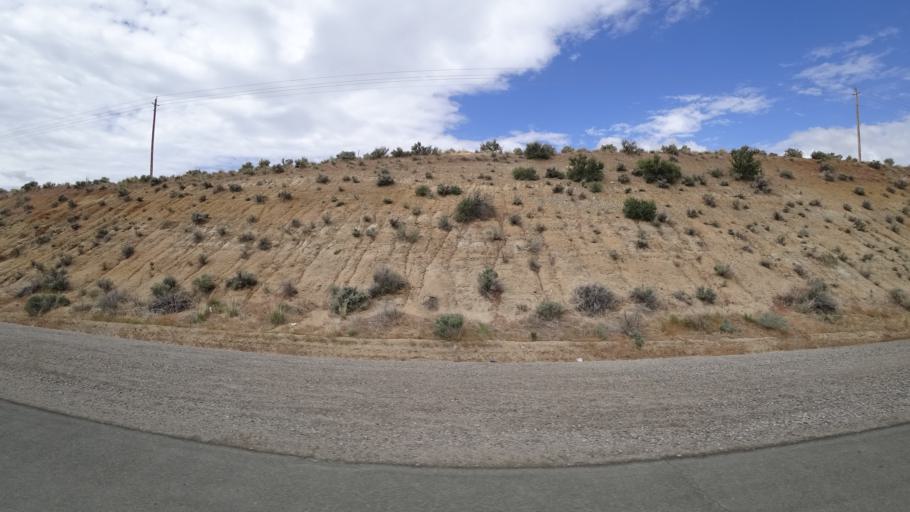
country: US
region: Nevada
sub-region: Douglas County
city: Indian Hills
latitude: 39.0834
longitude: -119.7771
